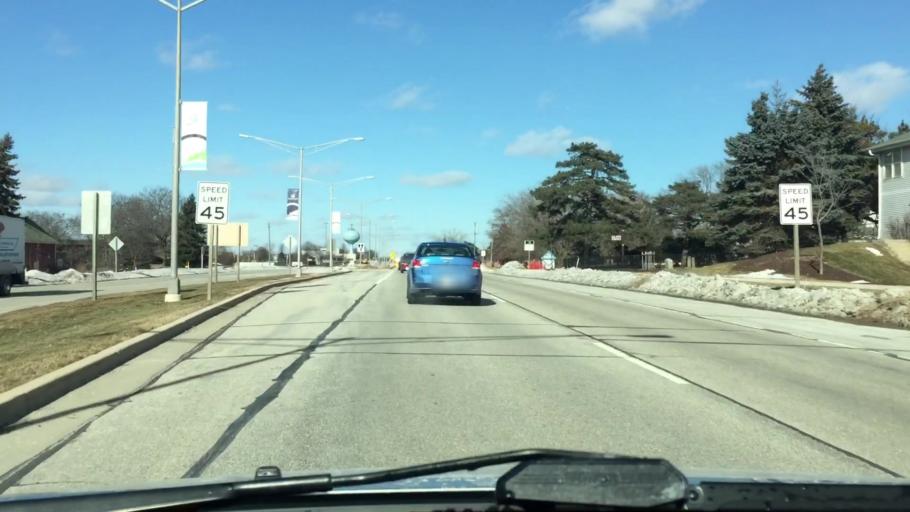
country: US
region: Wisconsin
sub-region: Milwaukee County
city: Oak Creek
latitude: 42.9030
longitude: -87.9114
